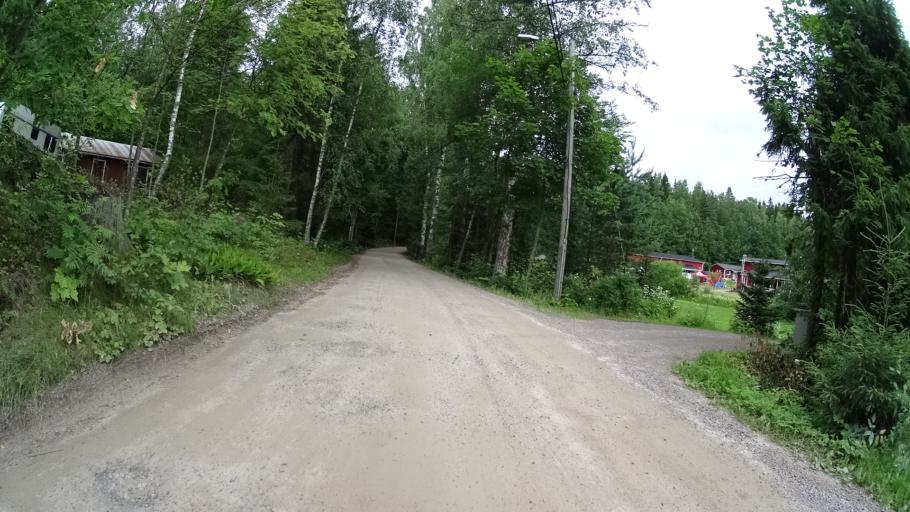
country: FI
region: Uusimaa
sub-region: Helsinki
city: Espoo
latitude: 60.2756
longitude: 24.6572
